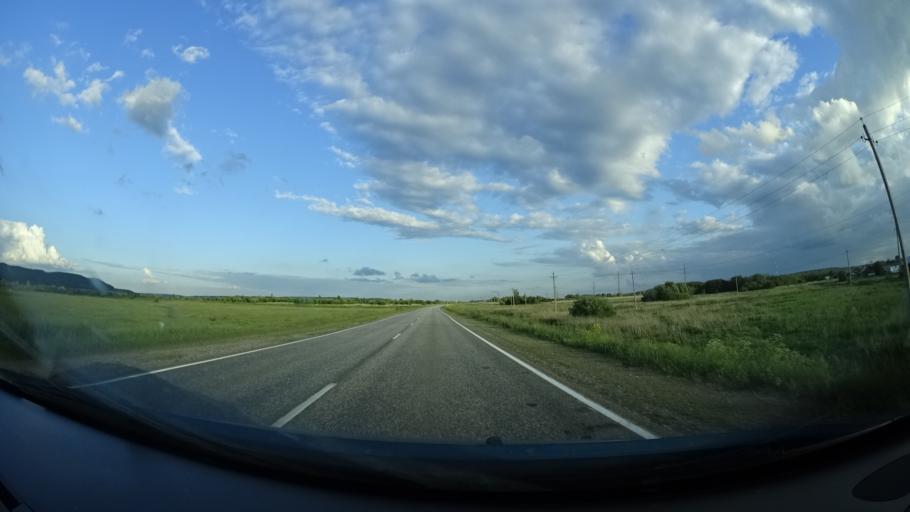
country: RU
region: Perm
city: Barda
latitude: 57.0881
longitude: 55.5389
